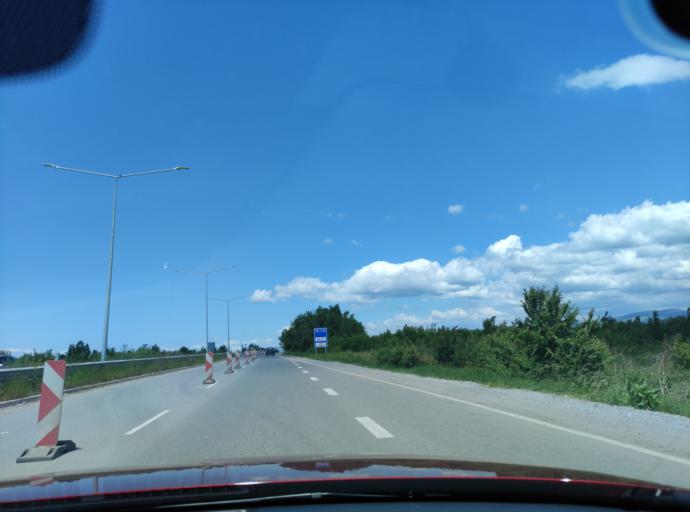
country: BG
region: Sofiya
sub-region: Obshtina Bozhurishte
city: Bozhurishte
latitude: 42.7606
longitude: 23.2661
